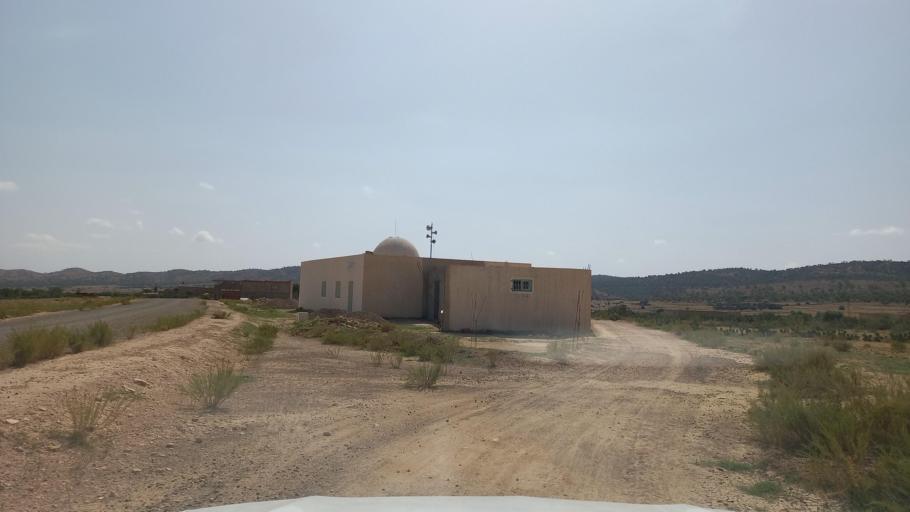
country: TN
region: Al Qasrayn
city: Sbiba
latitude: 35.3886
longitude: 8.9556
